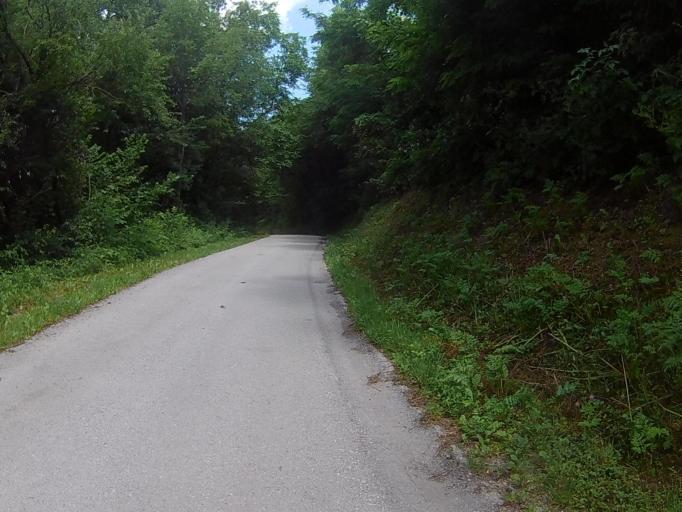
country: SI
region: Kungota
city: Zgornja Kungota
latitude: 46.6160
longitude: 15.6296
